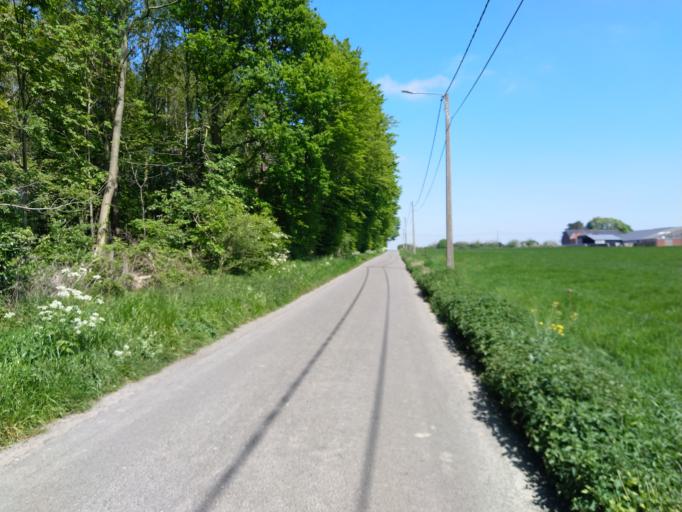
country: BE
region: Wallonia
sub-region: Province du Hainaut
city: Brugelette
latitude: 50.5506
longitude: 3.8502
